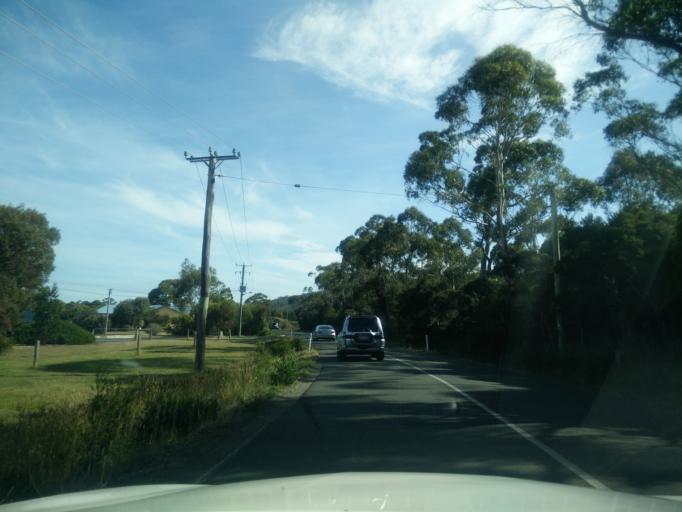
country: AU
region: Tasmania
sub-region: Break O'Day
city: St Helens
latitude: -41.2826
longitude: 148.2767
